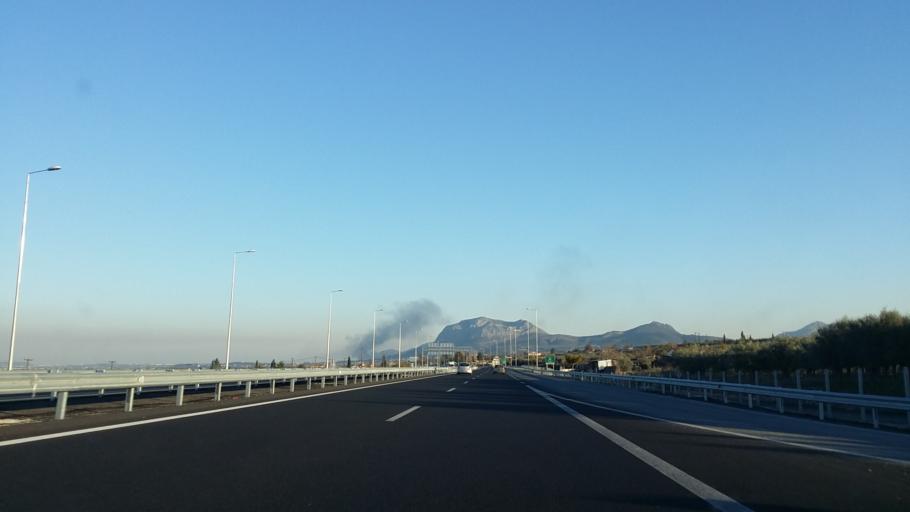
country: GR
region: Peloponnese
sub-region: Nomos Korinthias
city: Zevgolateio
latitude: 37.9281
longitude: 22.7911
